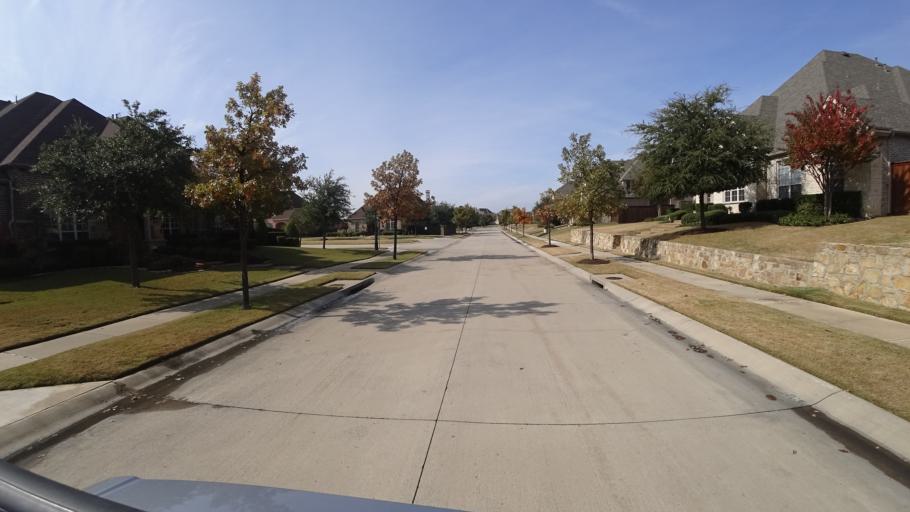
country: US
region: Texas
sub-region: Denton County
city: The Colony
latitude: 33.0427
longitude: -96.8885
